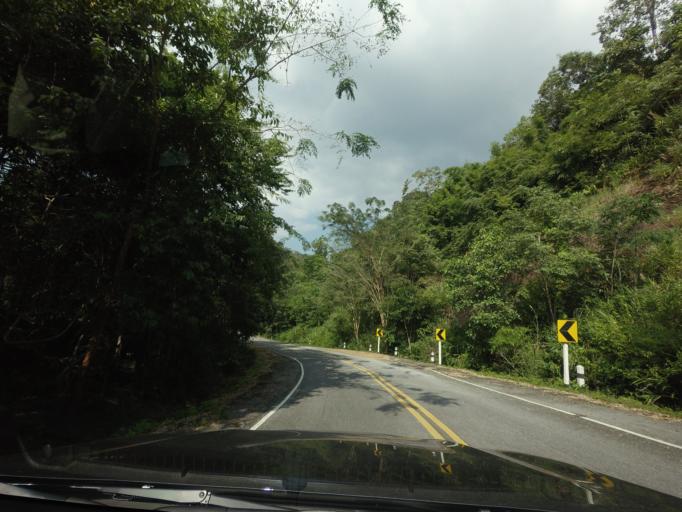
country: TH
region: Uttaradit
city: Ban Khok
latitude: 18.2648
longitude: 100.9930
